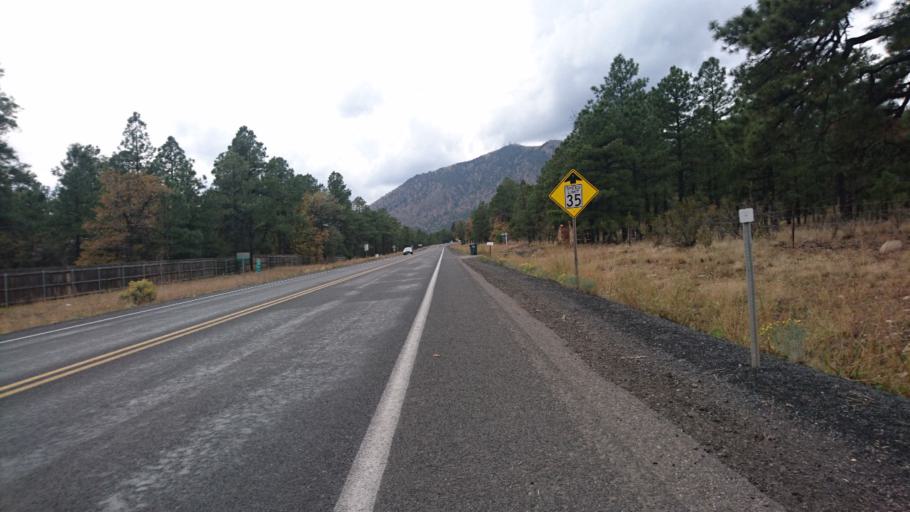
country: US
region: Arizona
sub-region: Coconino County
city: Flagstaff
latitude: 35.2457
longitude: -111.5591
